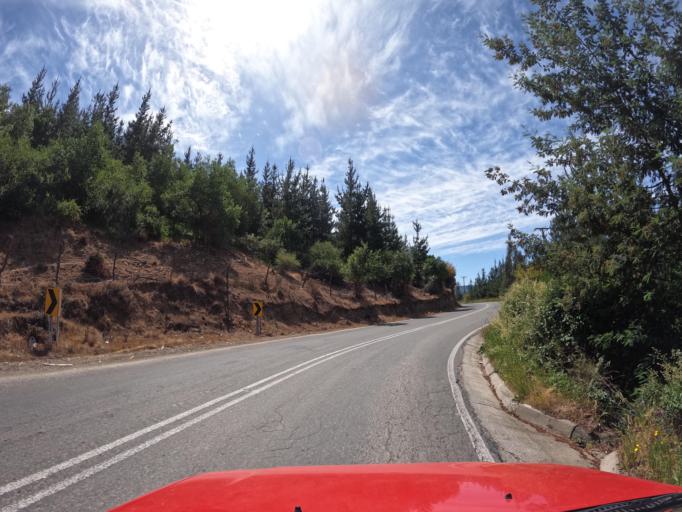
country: CL
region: Maule
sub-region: Provincia de Talca
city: Talca
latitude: -34.9916
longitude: -71.8104
